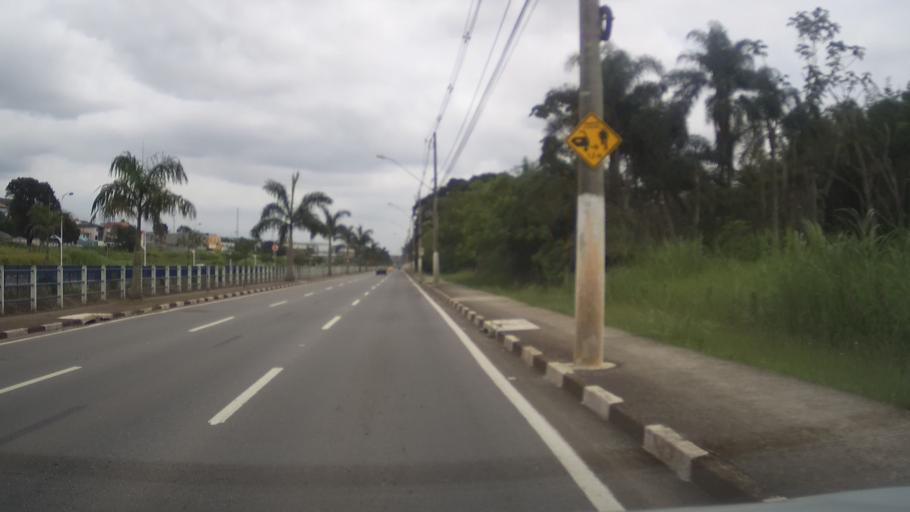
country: BR
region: Sao Paulo
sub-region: Aruja
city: Aruja
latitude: -23.3990
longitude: -46.3403
